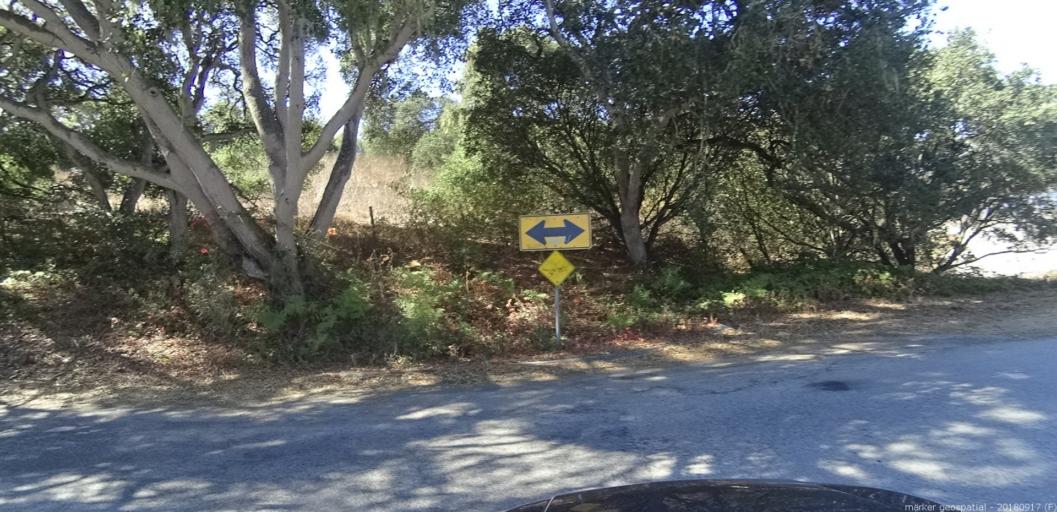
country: US
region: California
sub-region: Monterey County
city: Elkhorn
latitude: 36.8292
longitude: -121.7332
